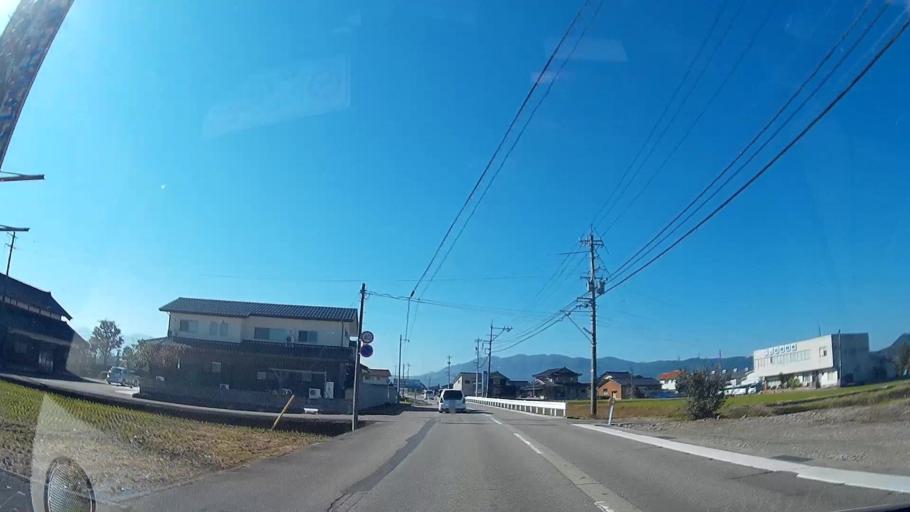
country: JP
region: Toyama
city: Nanto-shi
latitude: 36.5728
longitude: 136.8907
